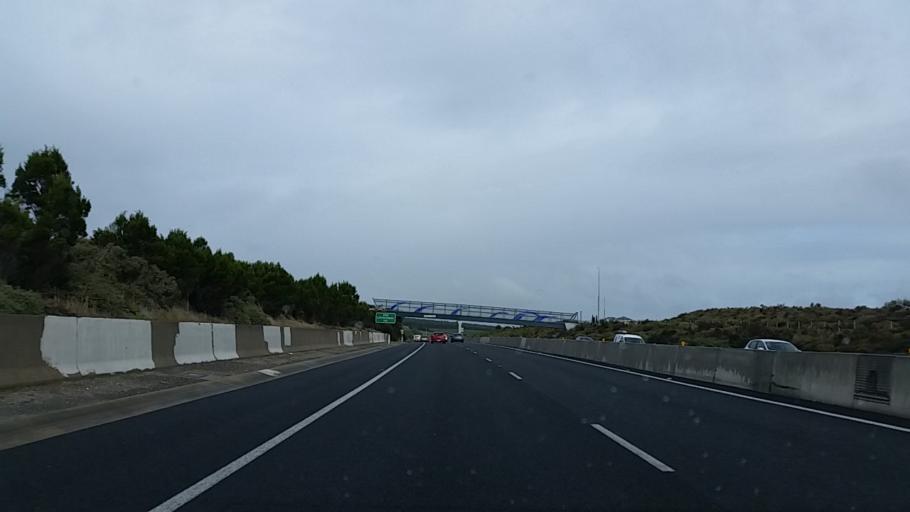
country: AU
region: South Australia
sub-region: Onkaparinga
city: Noarlunga Downs
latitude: -35.1558
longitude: 138.5061
